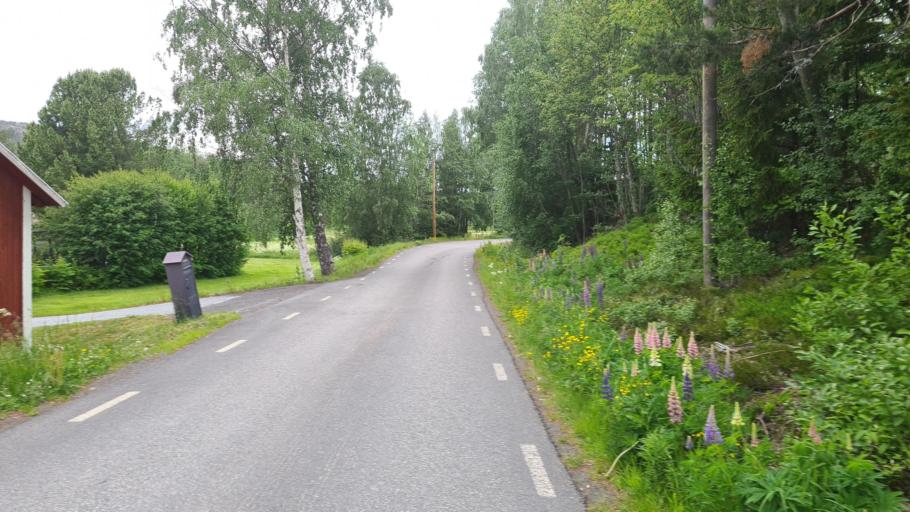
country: SE
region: Vaesternorrland
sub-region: Kramfors Kommun
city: Nordingra
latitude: 62.9742
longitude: 18.4247
